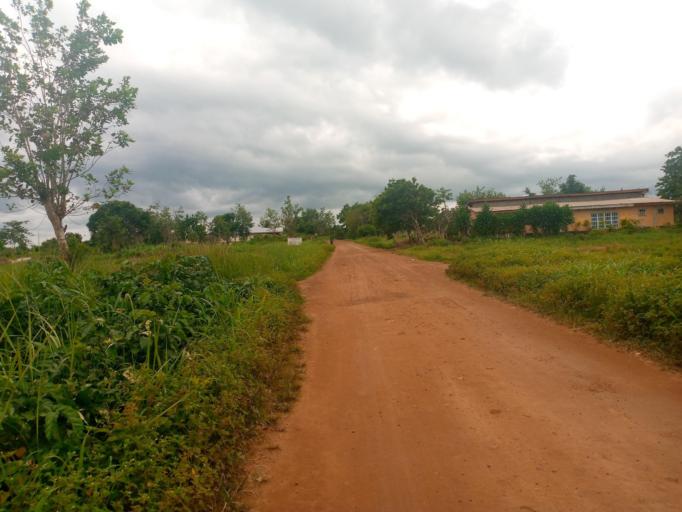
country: SL
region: Southern Province
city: Mogbwemo
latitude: 7.6157
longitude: -12.1781
